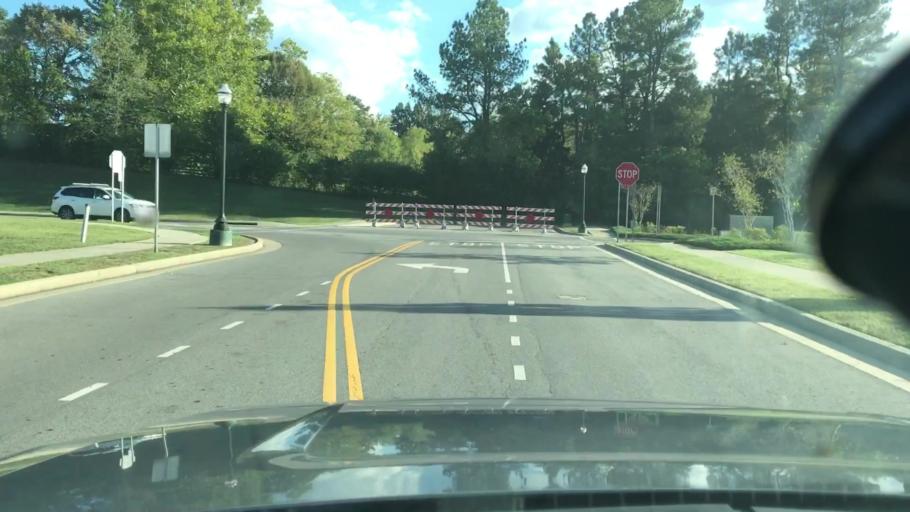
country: US
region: Tennessee
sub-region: Williamson County
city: Fairview
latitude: 35.9625
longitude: -87.1376
